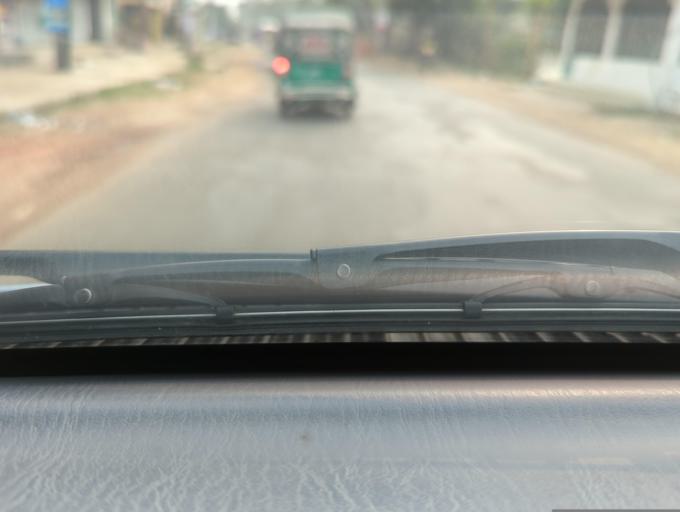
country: BD
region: Sylhet
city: Maulavi Bazar
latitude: 24.4906
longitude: 91.7473
